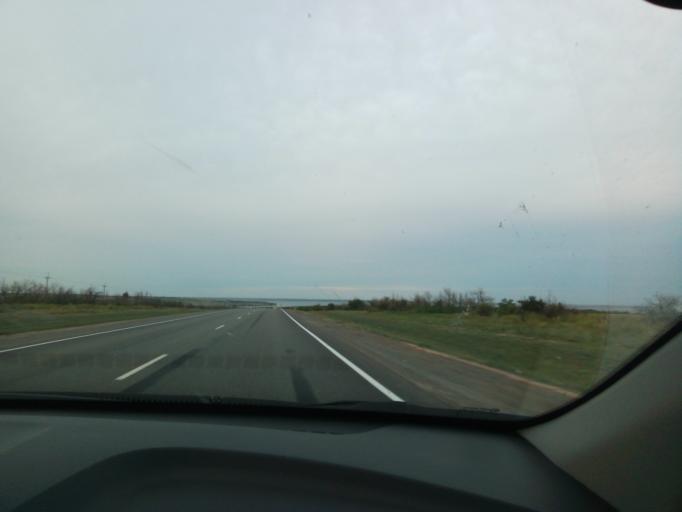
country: RU
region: Volgograd
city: Dubovka
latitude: 49.1561
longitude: 44.8458
